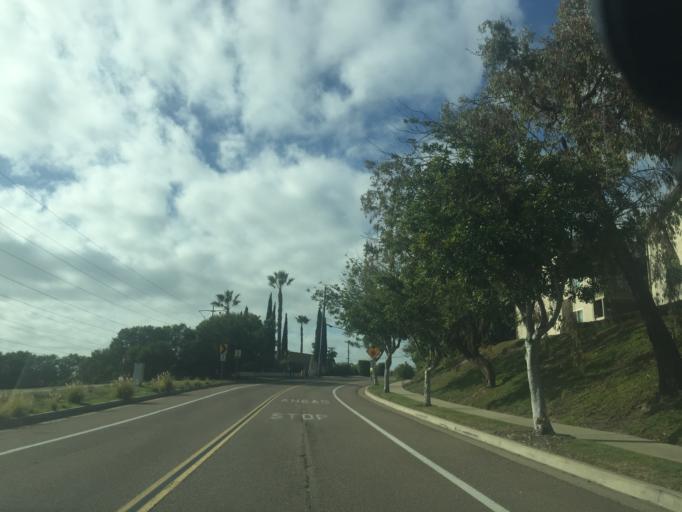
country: US
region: California
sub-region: San Diego County
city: San Diego
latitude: 32.7843
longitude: -117.1489
